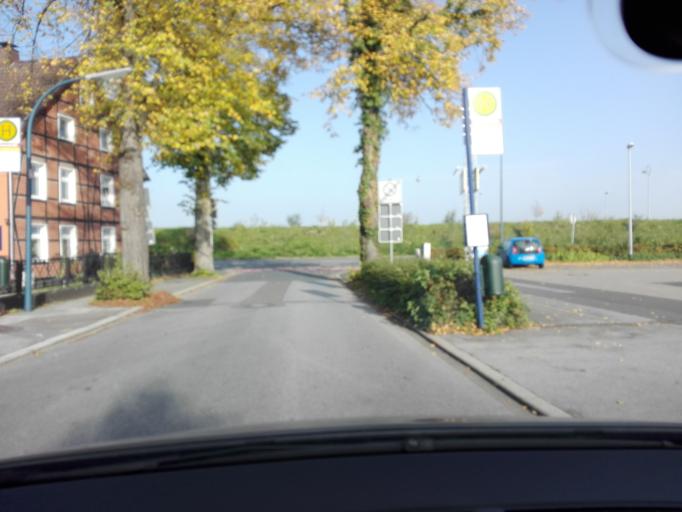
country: DE
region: North Rhine-Westphalia
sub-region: Regierungsbezirk Arnsberg
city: Holzwickede
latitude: 51.5175
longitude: 7.6242
